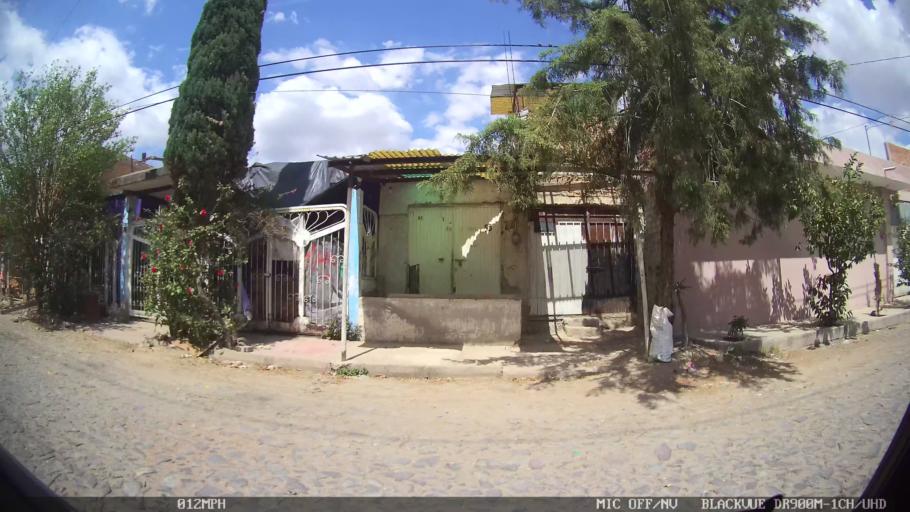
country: MX
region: Jalisco
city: Tlaquepaque
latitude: 20.6704
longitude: -103.2587
